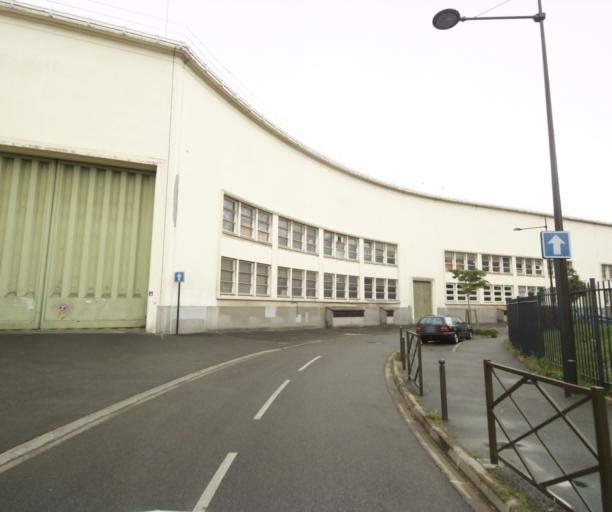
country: FR
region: Ile-de-France
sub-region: Departement du Val-d'Oise
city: Bezons
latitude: 48.9337
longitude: 2.2284
